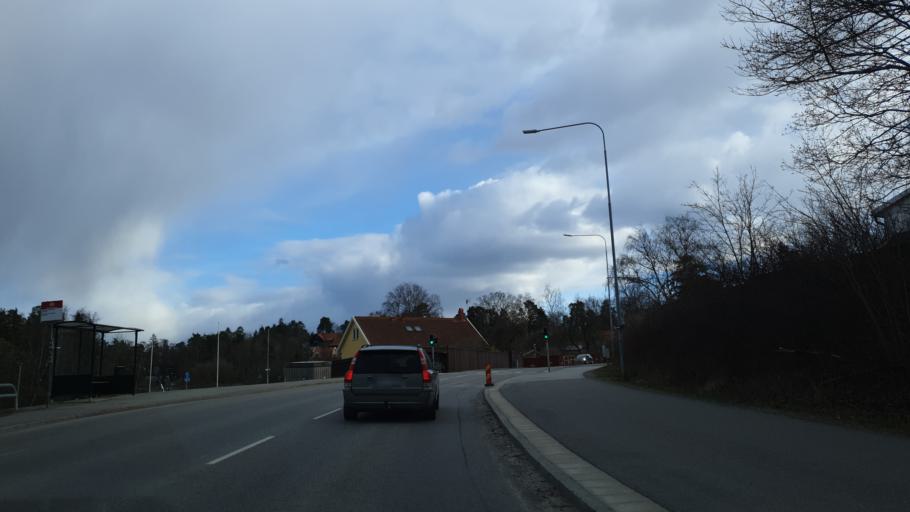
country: SE
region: Stockholm
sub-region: Lidingo
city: Lidingoe
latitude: 59.3731
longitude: 18.1330
